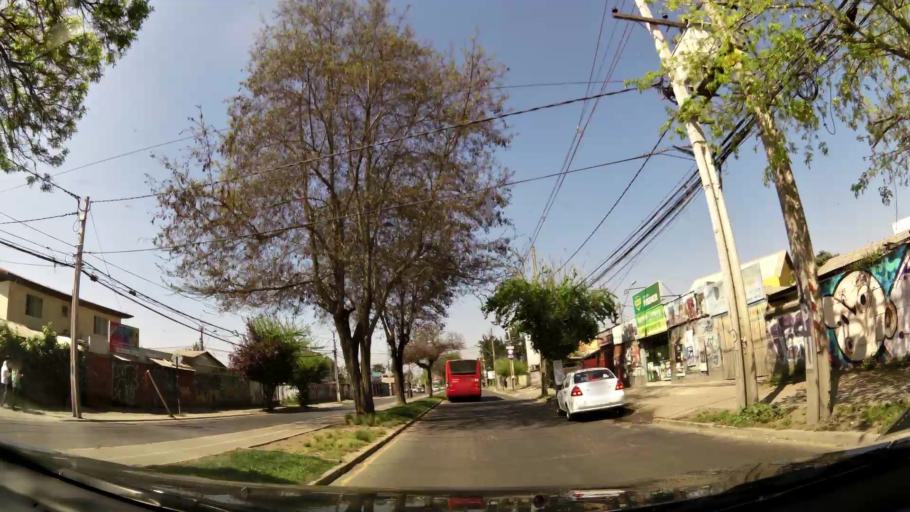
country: CL
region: Santiago Metropolitan
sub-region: Provincia de Santiago
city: Lo Prado
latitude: -33.3649
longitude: -70.7325
